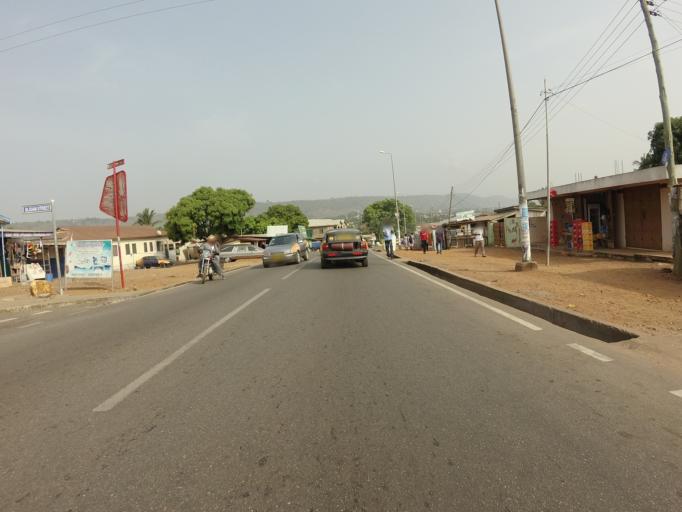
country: GH
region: Volta
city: Ho
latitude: 6.6093
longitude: 0.4748
